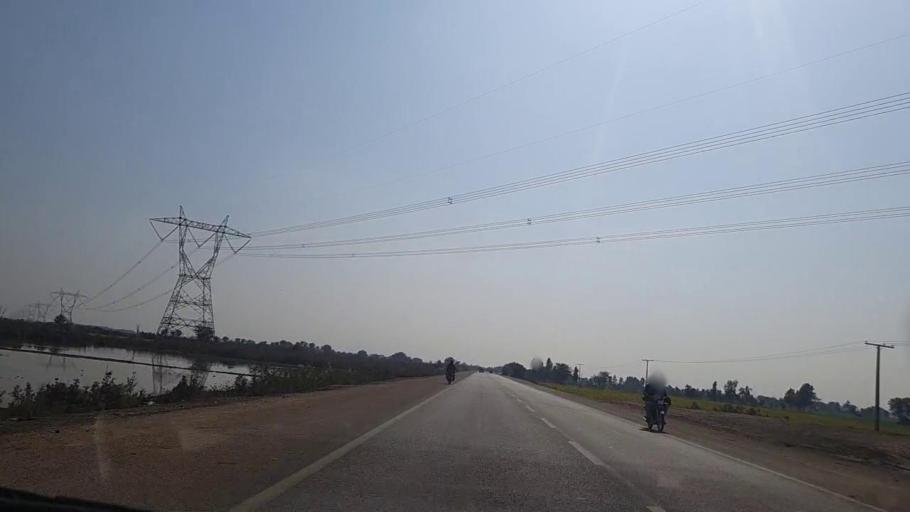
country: PK
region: Sindh
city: Sakrand
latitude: 26.0029
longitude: 68.3937
